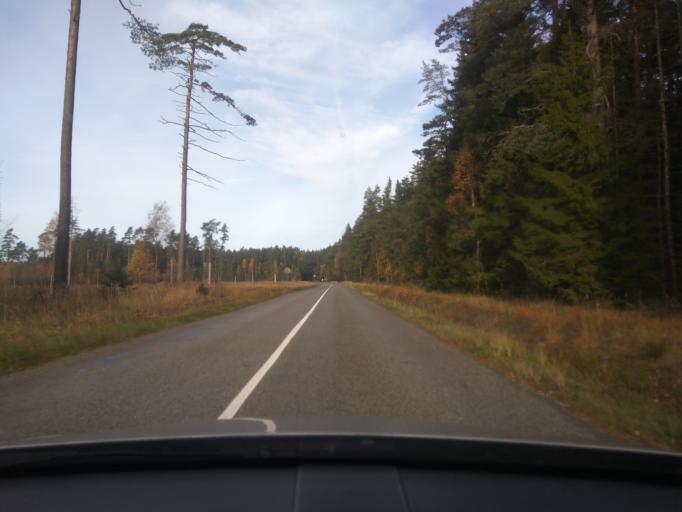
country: LV
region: Alsunga
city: Alsunga
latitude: 57.0011
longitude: 21.4675
